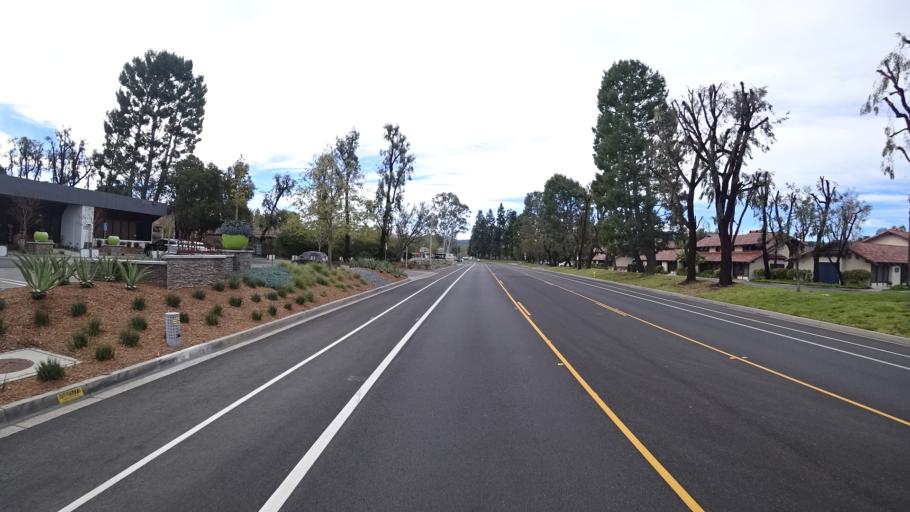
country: US
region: California
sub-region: Ventura County
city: Thousand Oaks
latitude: 34.1569
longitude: -118.8287
